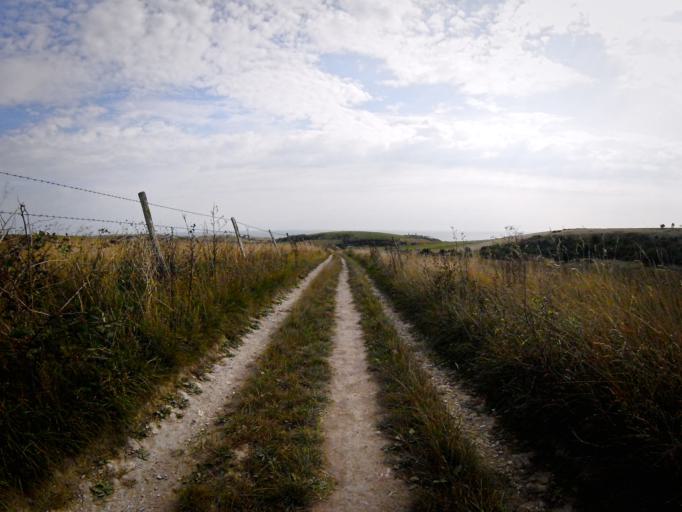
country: GB
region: England
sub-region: Brighton and Hove
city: Rottingdean
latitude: 50.8270
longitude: -0.0866
